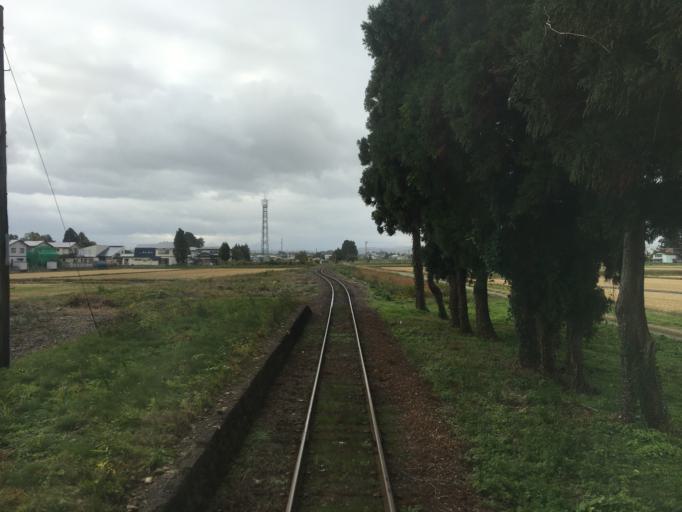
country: JP
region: Yamagata
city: Nagai
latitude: 38.0765
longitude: 140.0296
